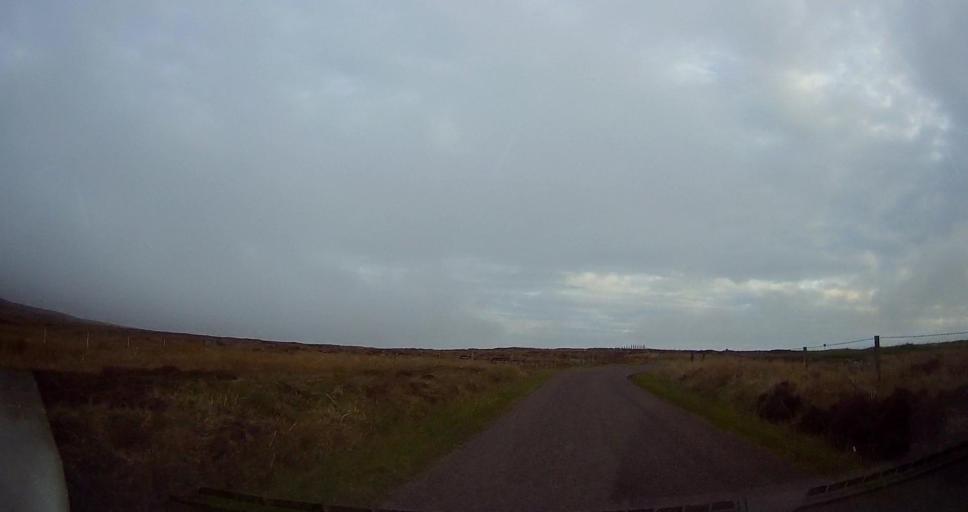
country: GB
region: Scotland
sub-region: Orkney Islands
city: Stromness
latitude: 59.1031
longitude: -3.1354
